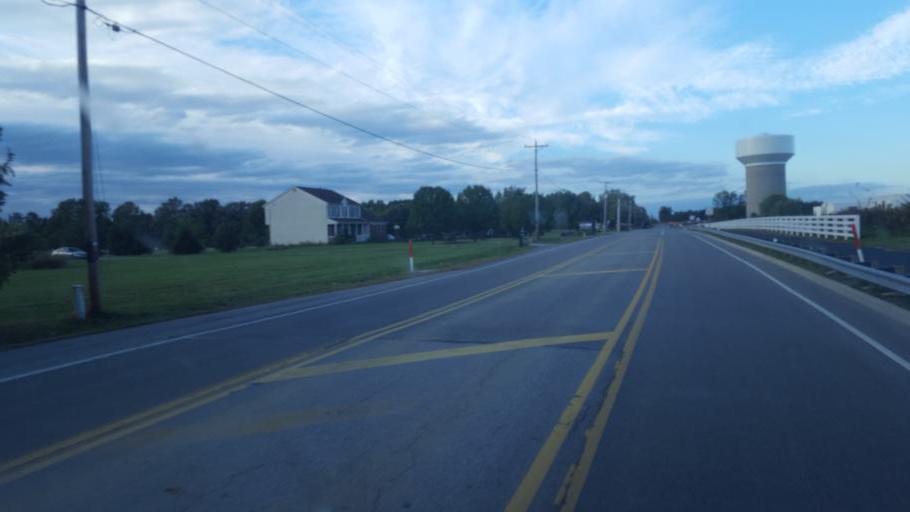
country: US
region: Ohio
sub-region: Franklin County
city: New Albany
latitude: 40.0901
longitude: -82.7544
